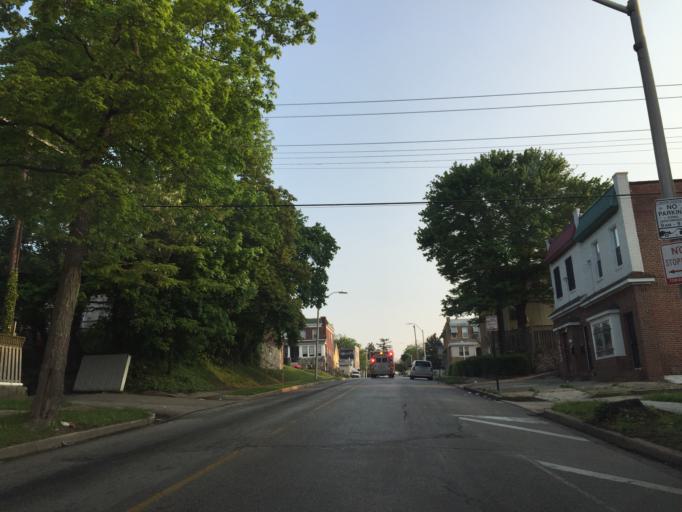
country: US
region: Maryland
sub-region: Baltimore County
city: Woodlawn
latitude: 39.3145
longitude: -76.6727
